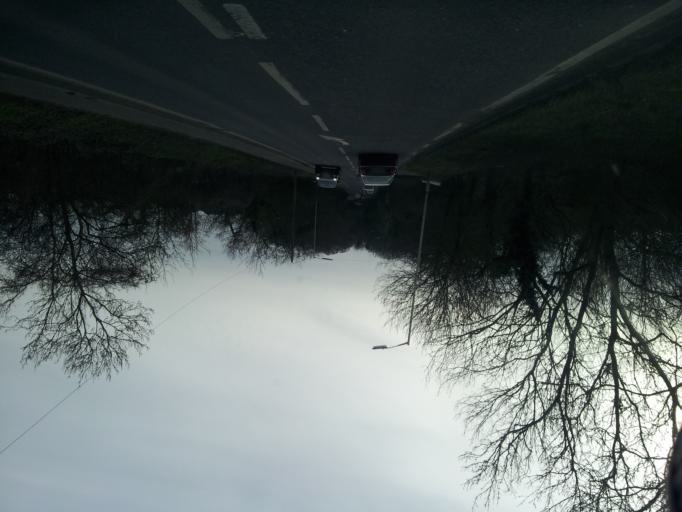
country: GB
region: England
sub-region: Hertfordshire
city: Borehamwood
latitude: 51.6444
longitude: -0.2749
